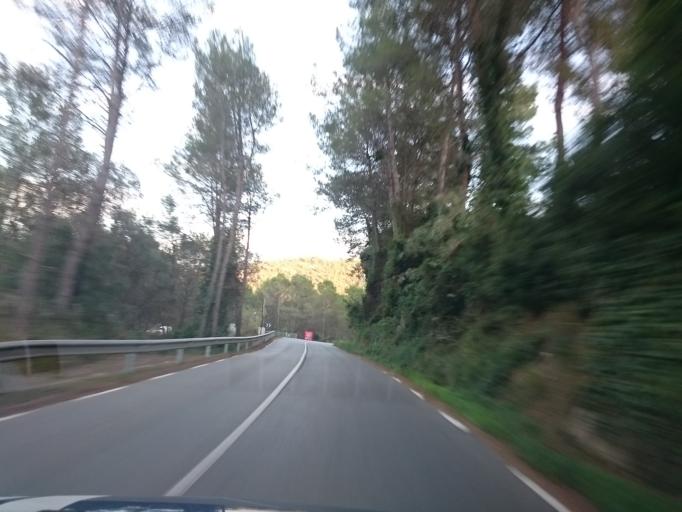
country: ES
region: Catalonia
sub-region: Provincia de Barcelona
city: Sant Pere de Ribes
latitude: 41.2965
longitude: 1.7805
